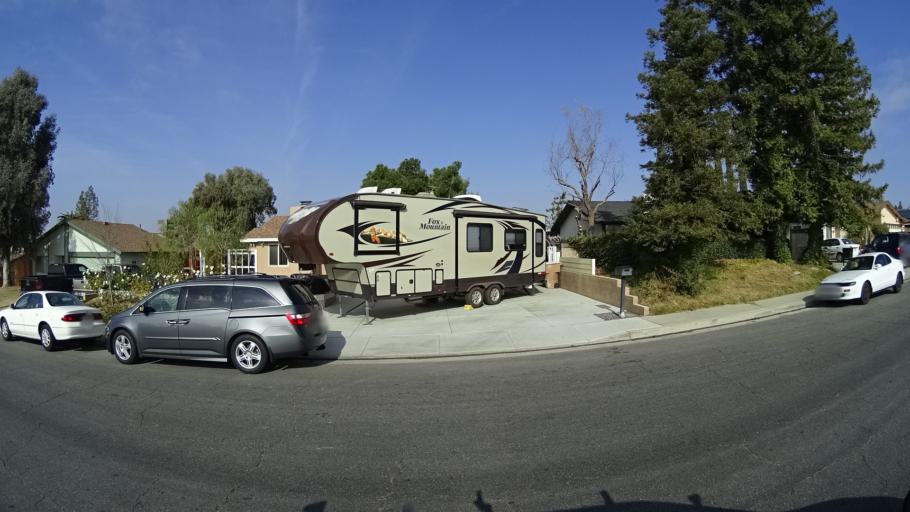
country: US
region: California
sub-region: Kern County
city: Oildale
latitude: 35.3991
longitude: -118.9292
